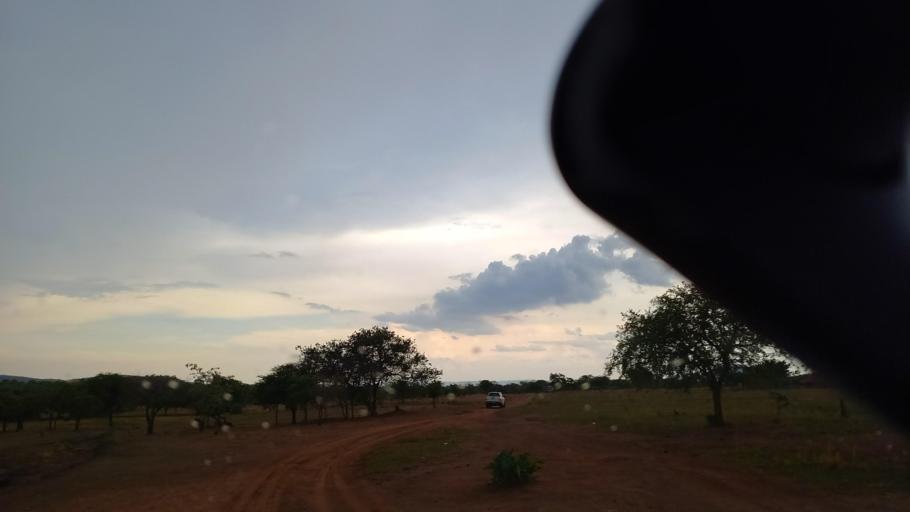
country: ZM
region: Lusaka
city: Kafue
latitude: -15.9755
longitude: 28.2533
